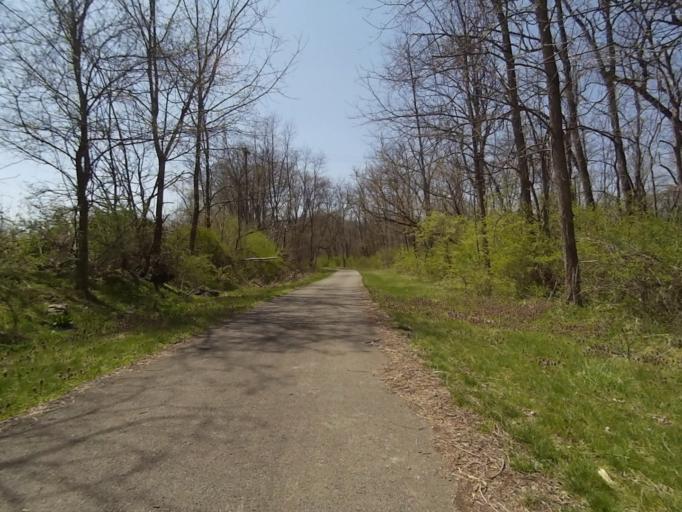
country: US
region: Pennsylvania
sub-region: Blair County
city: Williamsburg
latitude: 40.4740
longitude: -78.1970
